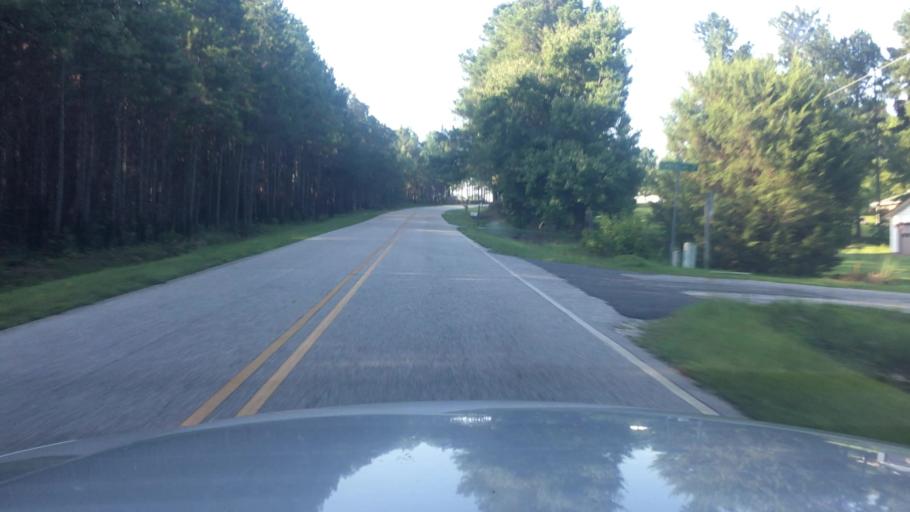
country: US
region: North Carolina
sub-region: Cumberland County
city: Spring Lake
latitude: 35.2179
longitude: -78.8938
